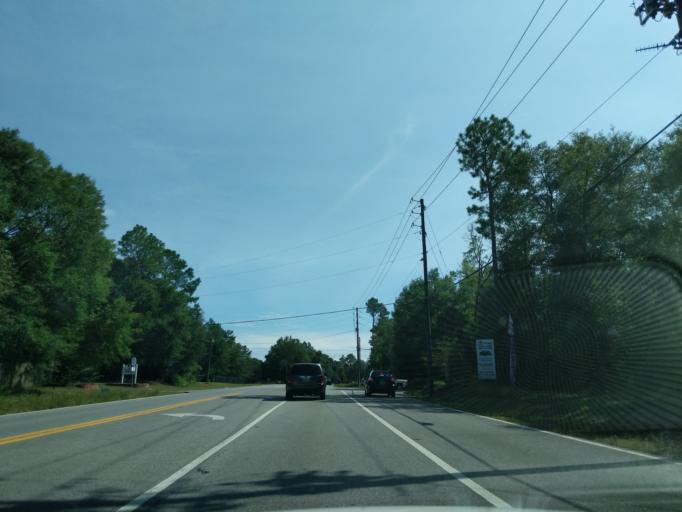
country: US
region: Florida
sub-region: Okaloosa County
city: Crestview
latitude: 30.7269
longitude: -86.6172
